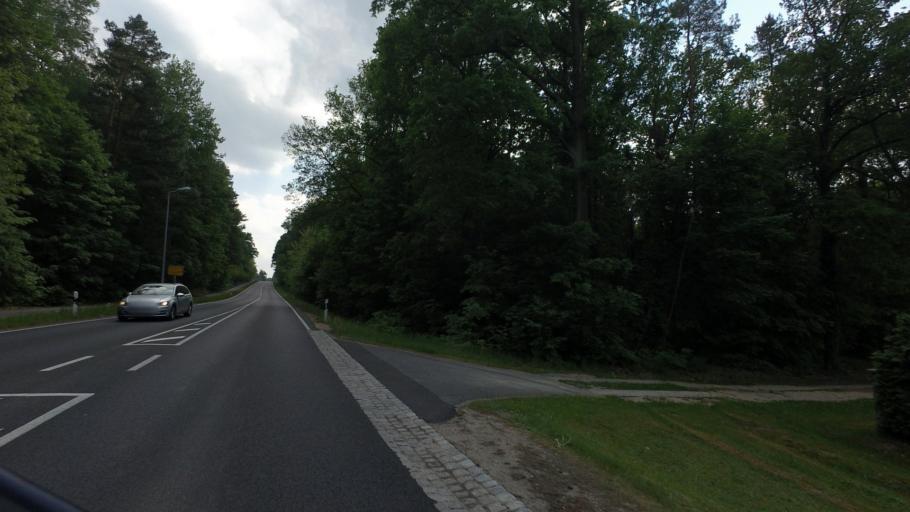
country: DE
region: Saxony
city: Rietschen
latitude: 51.3870
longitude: 14.7859
